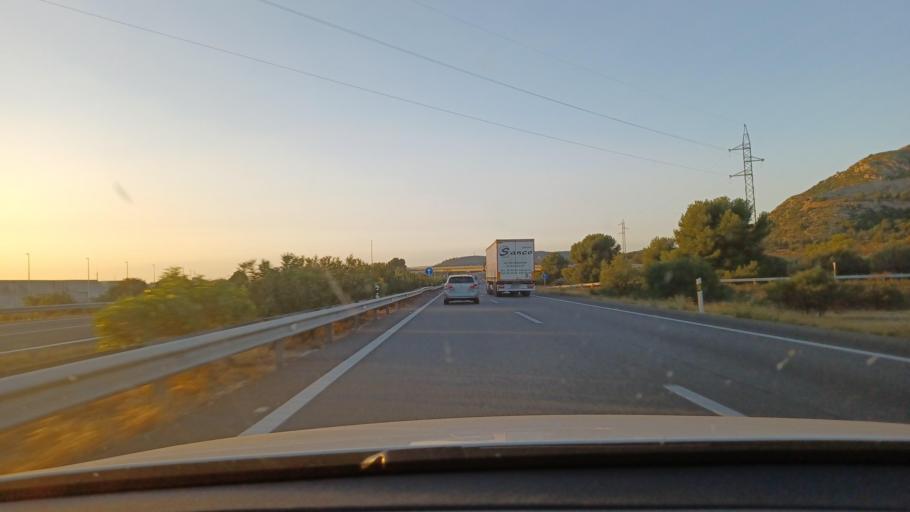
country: ES
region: Valencia
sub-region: Provincia de Castello
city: Orpesa/Oropesa del Mar
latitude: 40.1101
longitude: 0.1309
